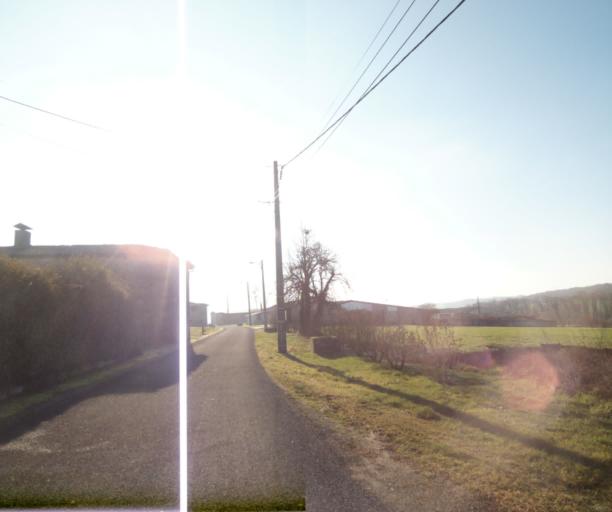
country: FR
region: Champagne-Ardenne
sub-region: Departement de la Haute-Marne
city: Wassy
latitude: 48.5245
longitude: 4.9927
